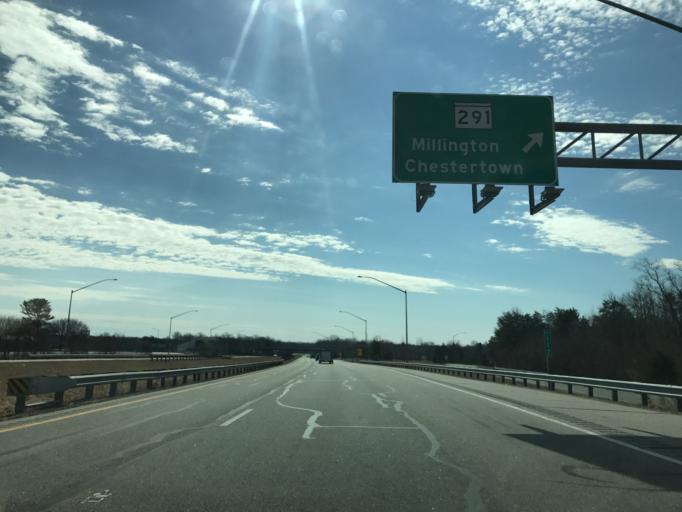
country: US
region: Maryland
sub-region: Queen Anne's County
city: Kingstown
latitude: 39.2687
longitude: -75.8639
